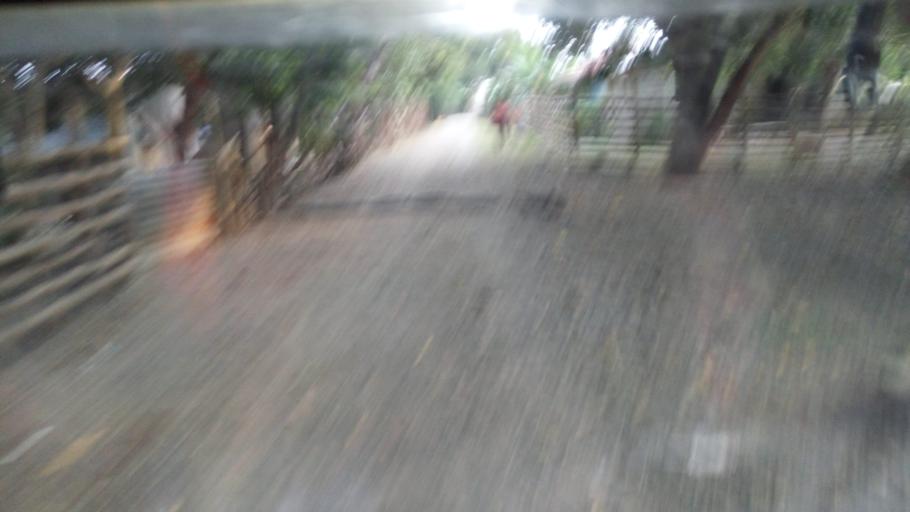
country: PH
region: Ilocos
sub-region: Province of La Union
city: Damortis
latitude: 16.2480
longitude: 120.4037
